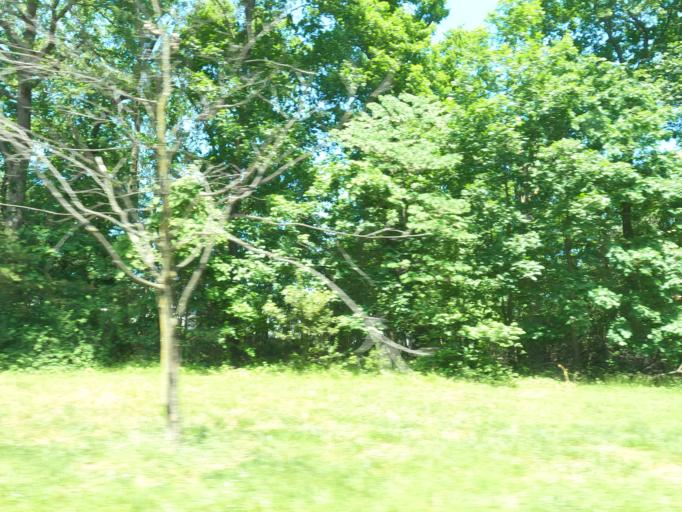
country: US
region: Maryland
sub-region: Howard County
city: Savage
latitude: 39.1771
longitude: -76.8081
